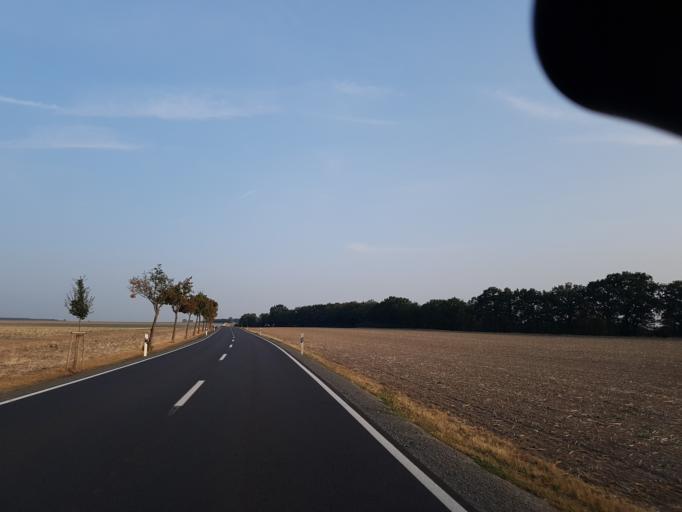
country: DE
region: Saxony
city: Zinna
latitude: 51.5839
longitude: 12.9570
